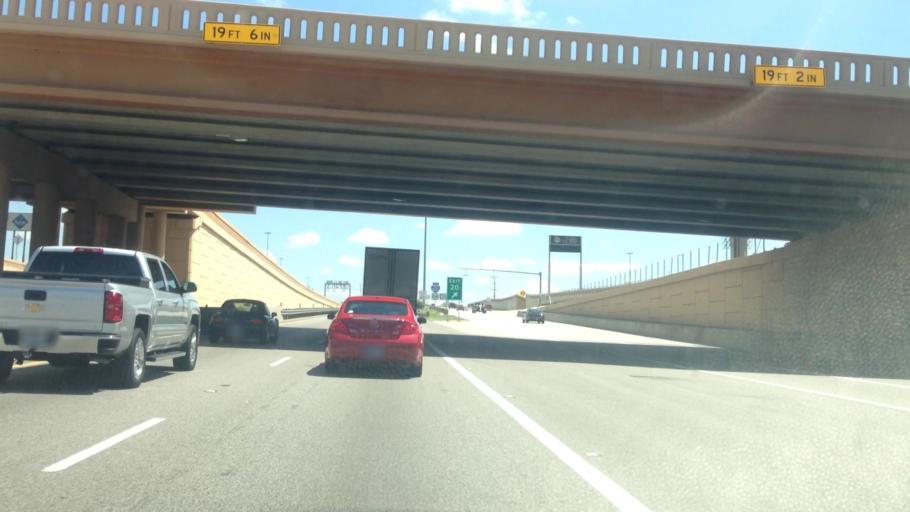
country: US
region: Texas
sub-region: Tarrant County
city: Watauga
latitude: 32.8399
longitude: -97.2518
